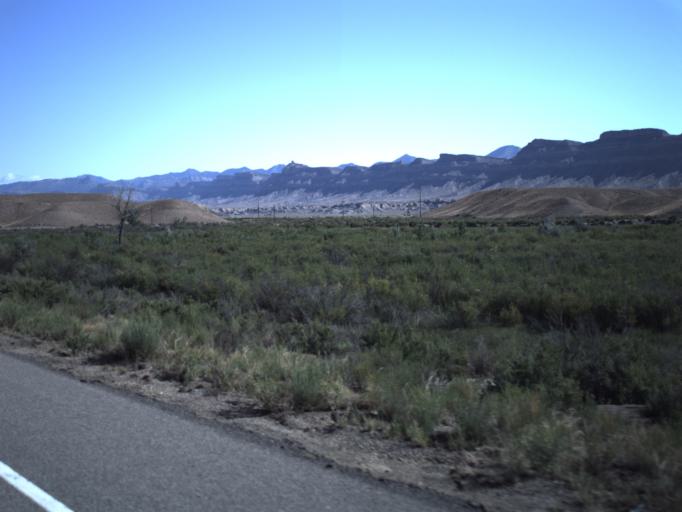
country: US
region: Utah
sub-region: Carbon County
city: East Carbon City
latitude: 39.2622
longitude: -110.3422
